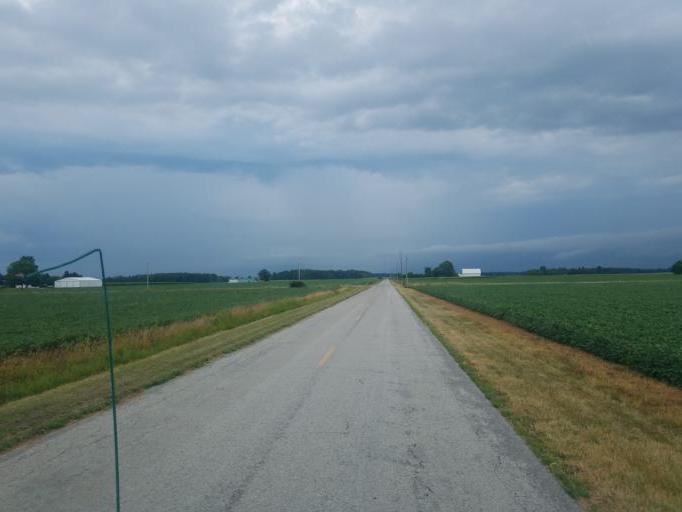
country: US
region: Ohio
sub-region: Defiance County
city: Hicksville
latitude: 41.2372
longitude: -84.7935
